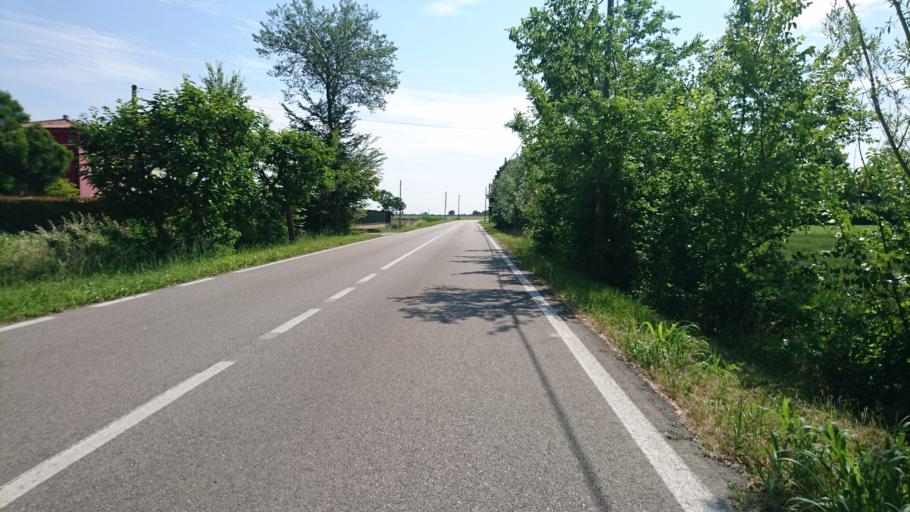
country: IT
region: Veneto
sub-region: Provincia di Padova
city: Megliadino San Vitale
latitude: 45.1926
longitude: 11.5339
